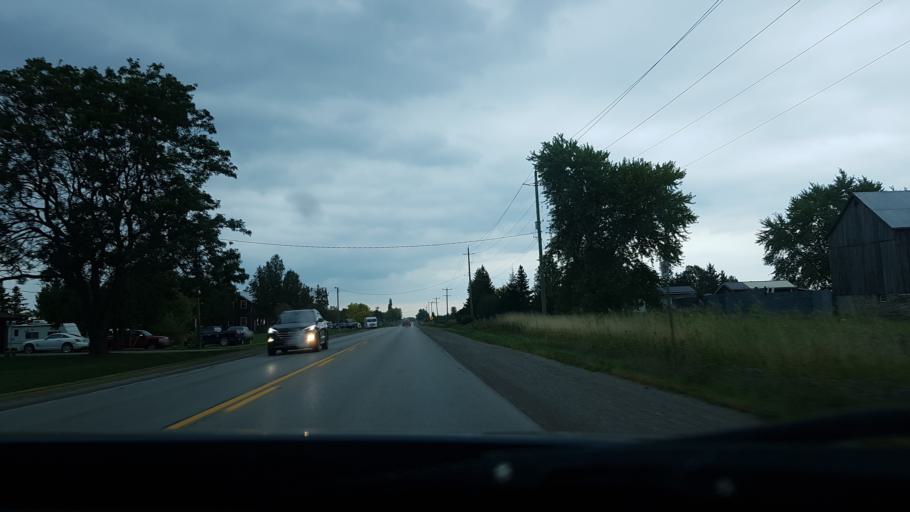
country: CA
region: Ontario
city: Omemee
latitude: 44.3656
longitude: -78.6918
